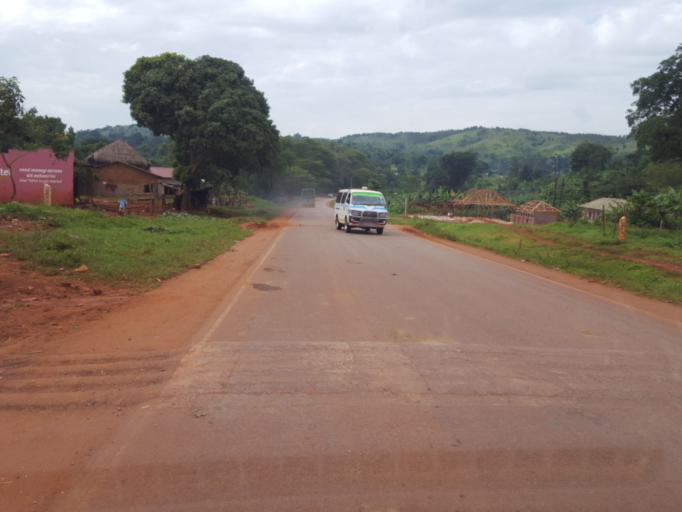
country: UG
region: Central Region
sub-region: Mityana District
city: Mityana
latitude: 0.6320
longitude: 32.1133
